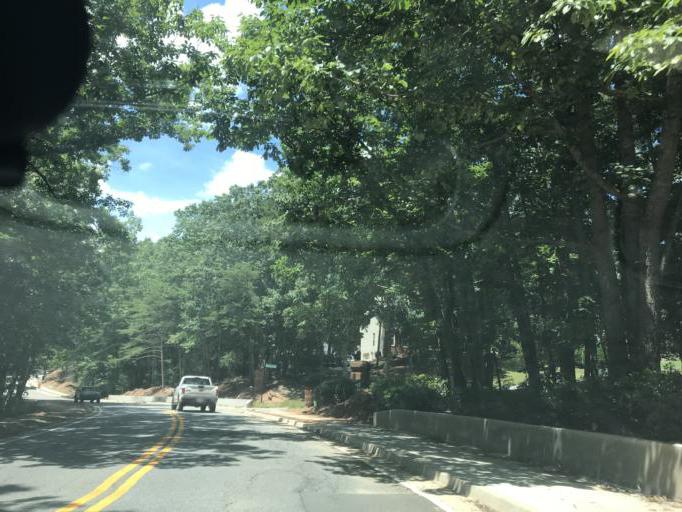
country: US
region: Georgia
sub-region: Forsyth County
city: Cumming
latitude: 34.1813
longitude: -84.1089
